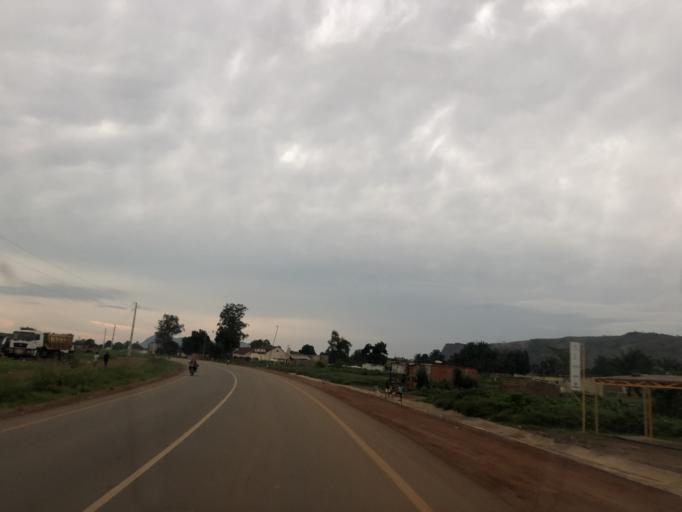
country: AO
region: Cuanza Sul
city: Uacu Cungo
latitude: -11.3491
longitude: 15.1056
